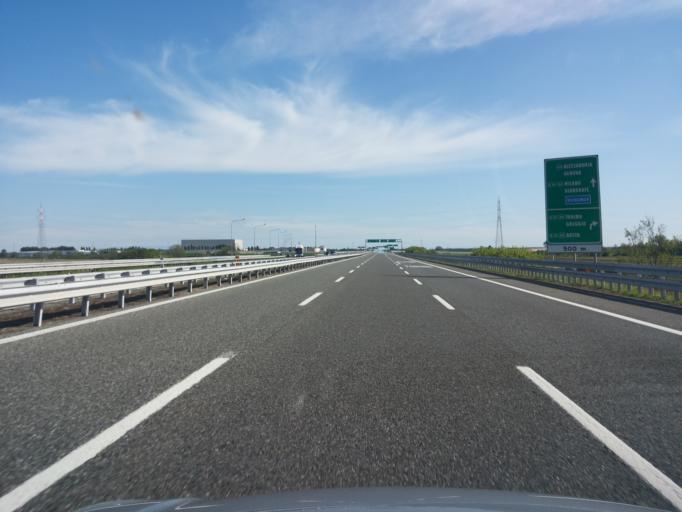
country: IT
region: Piedmont
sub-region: Provincia di Novara
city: Vicolungo
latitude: 45.4732
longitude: 8.4476
